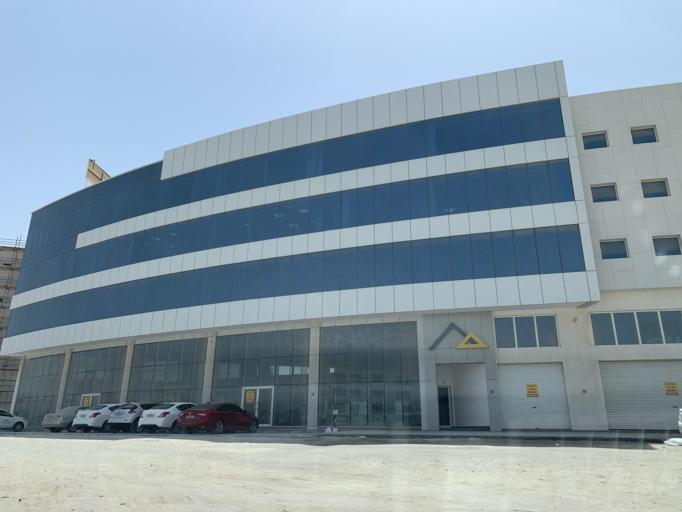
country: BH
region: Northern
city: Madinat `Isa
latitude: 26.1895
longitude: 50.5507
